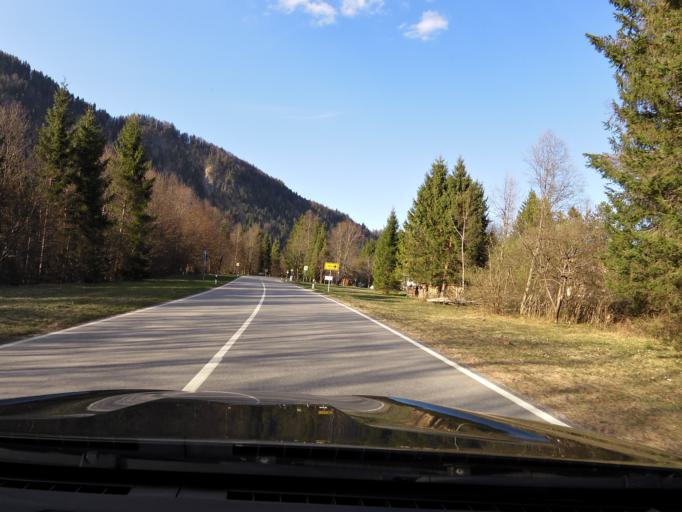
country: DE
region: Bavaria
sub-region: Upper Bavaria
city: Jachenau
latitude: 47.5694
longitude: 11.5298
